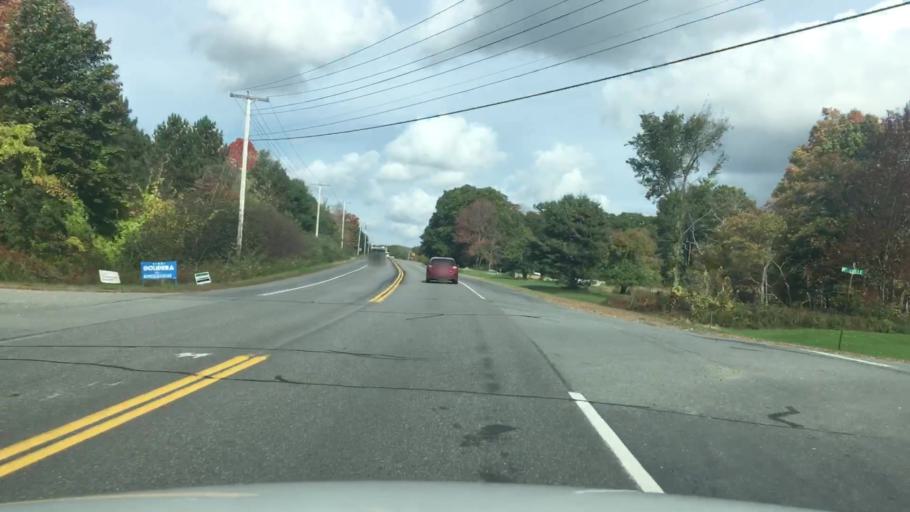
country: US
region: Maine
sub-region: Knox County
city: Rockport
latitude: 44.1563
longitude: -69.1146
